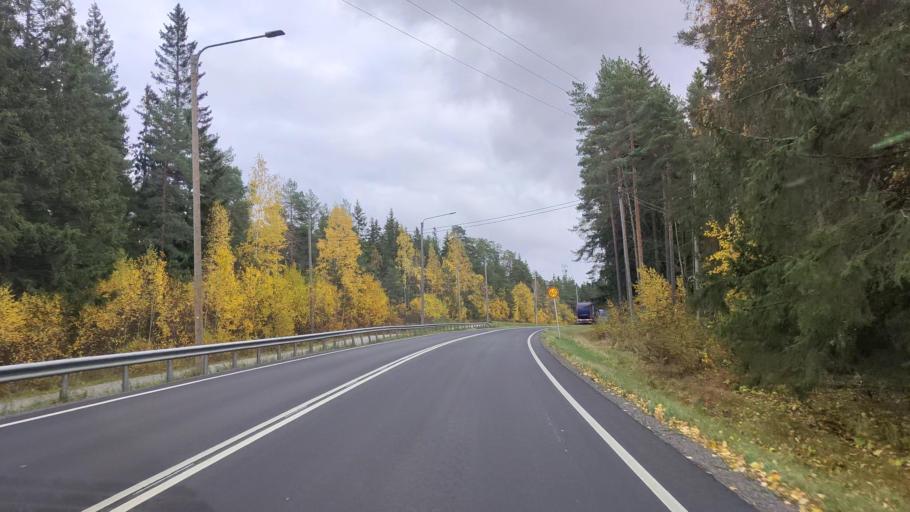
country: FI
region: Varsinais-Suomi
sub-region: Turku
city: Kaarina
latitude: 60.4601
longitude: 22.3625
